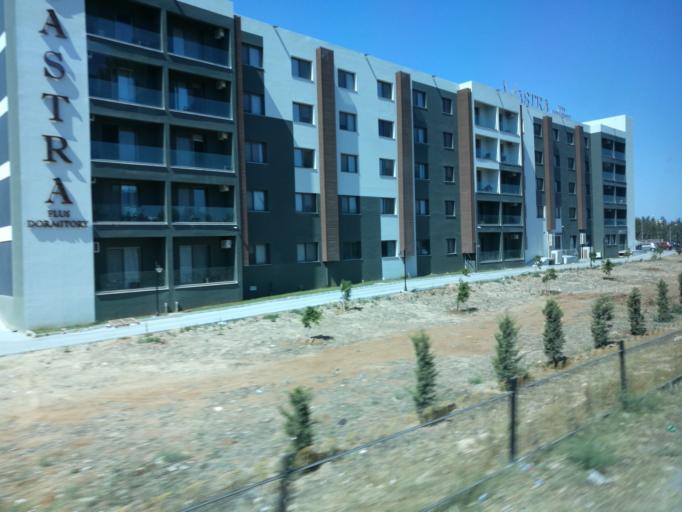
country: CY
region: Ammochostos
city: Famagusta
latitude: 35.1406
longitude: 33.9078
